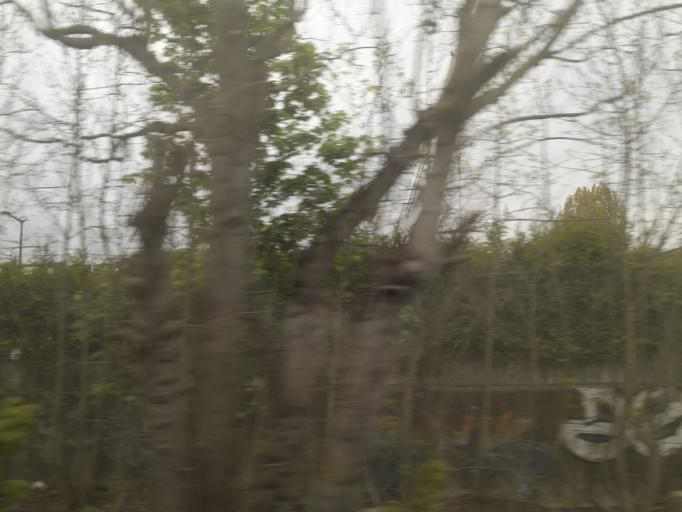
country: FR
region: Ile-de-France
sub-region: Departement du Val-de-Marne
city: Fresnes
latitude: 48.7479
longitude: 2.3146
